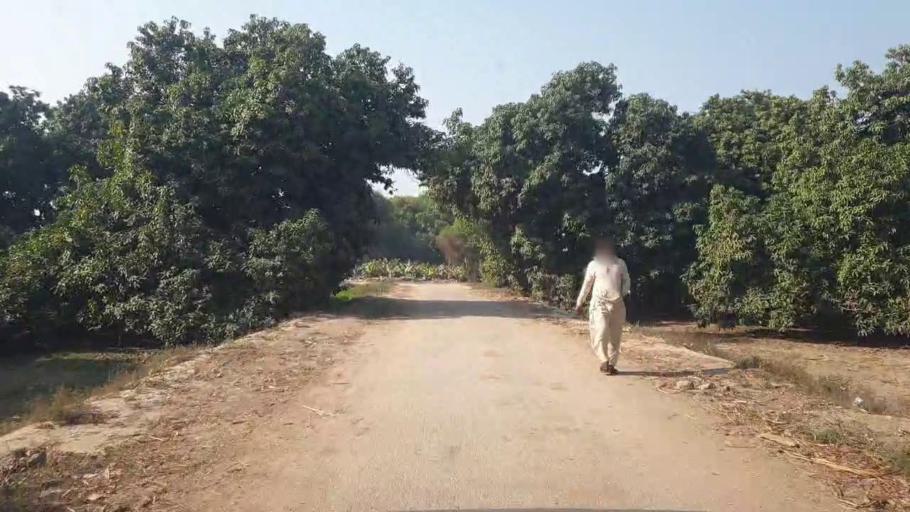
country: PK
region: Sindh
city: Tando Allahyar
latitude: 25.4666
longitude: 68.7631
